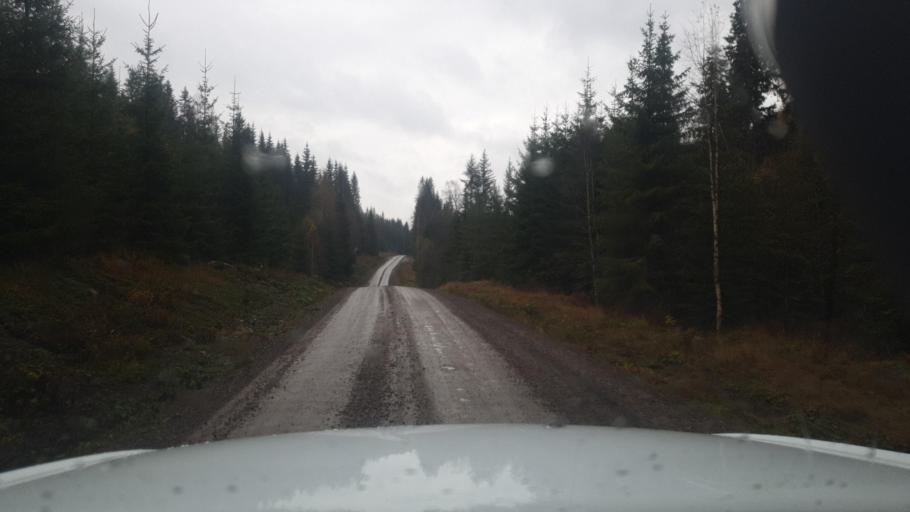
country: SE
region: Vaermland
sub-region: Eda Kommun
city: Charlottenberg
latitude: 60.0398
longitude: 12.5829
